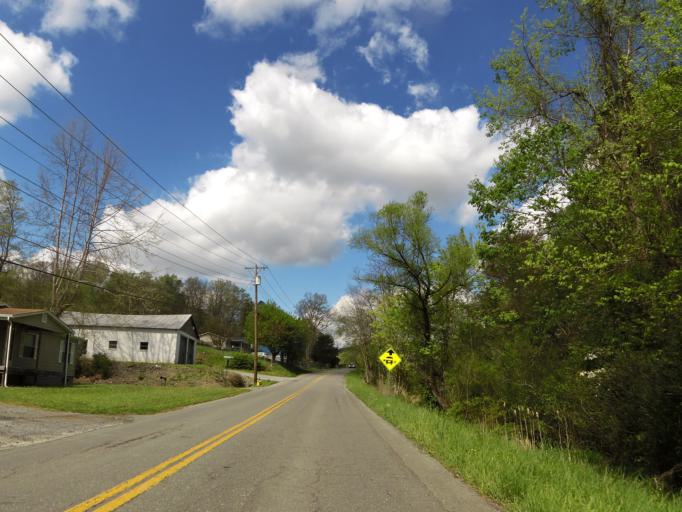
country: US
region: Kentucky
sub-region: Bell County
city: Middlesboro
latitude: 36.6302
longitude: -83.7328
